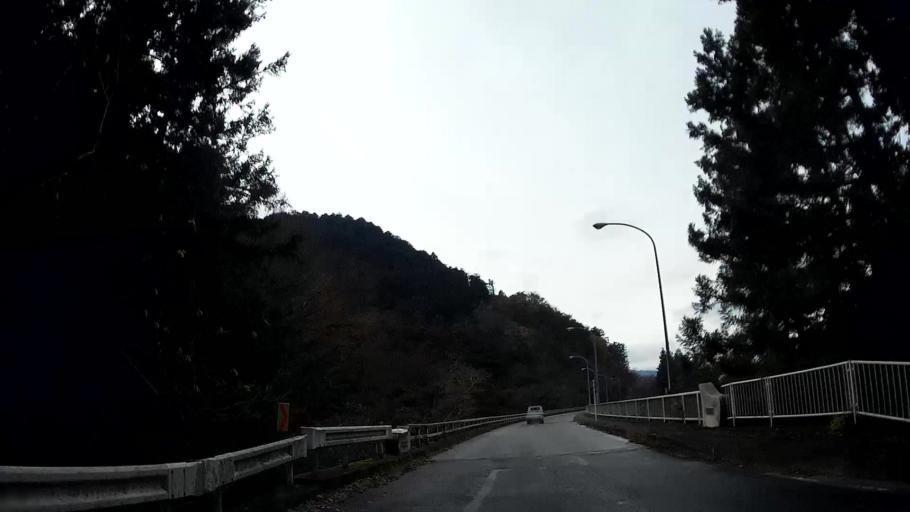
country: JP
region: Saitama
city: Chichibu
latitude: 35.9613
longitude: 139.0606
